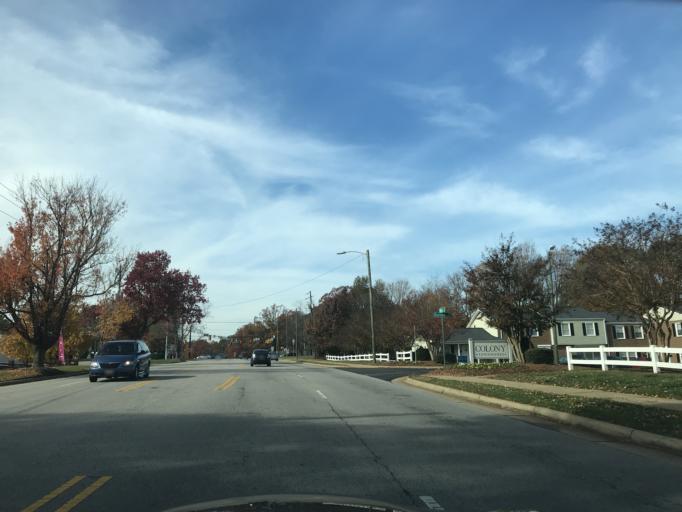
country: US
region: North Carolina
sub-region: Wake County
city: West Raleigh
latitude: 35.8556
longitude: -78.6392
